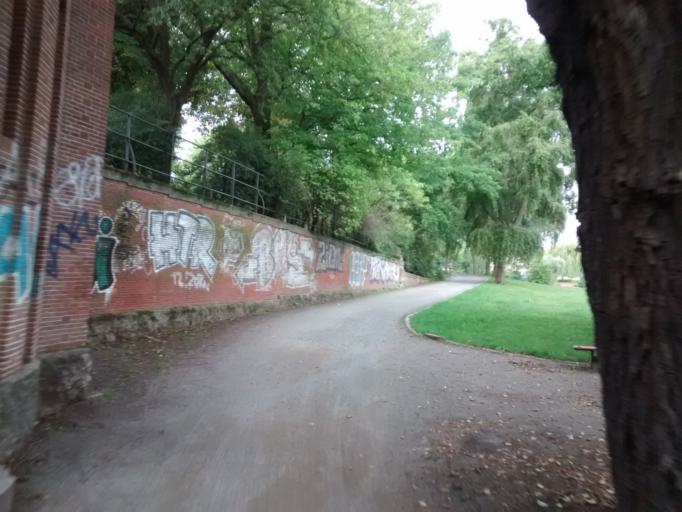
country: DE
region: Berlin
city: Moabit
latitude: 52.5195
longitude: 13.3188
